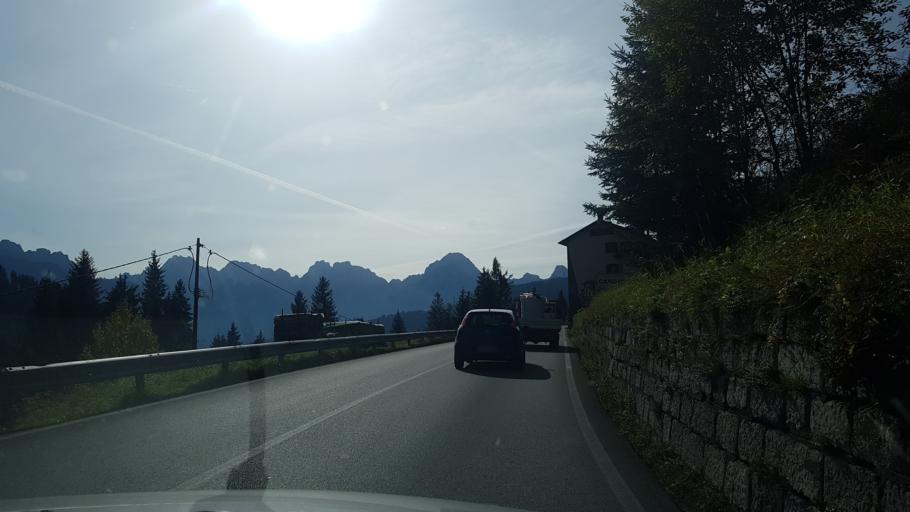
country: IT
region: Veneto
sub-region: Provincia di Belluno
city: Candide
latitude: 46.5971
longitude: 12.5214
